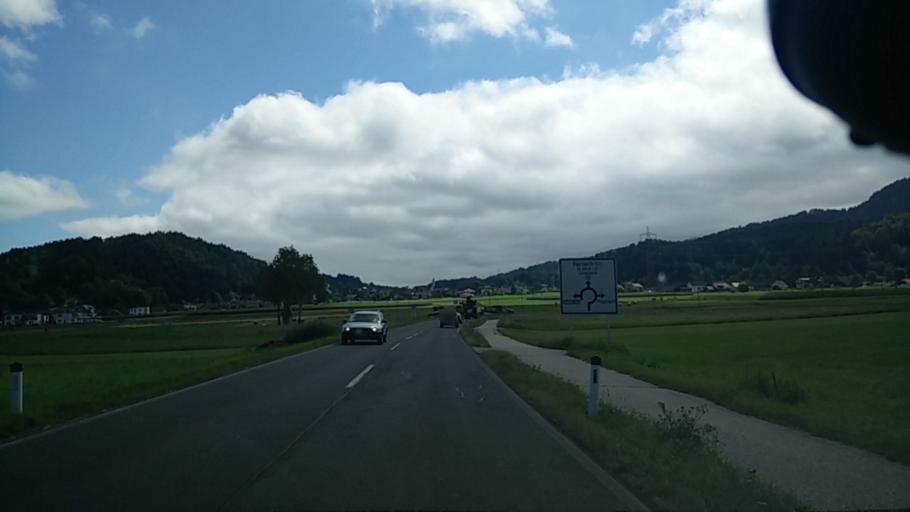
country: AT
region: Carinthia
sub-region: Politischer Bezirk Villach Land
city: Finkenstein am Faaker See
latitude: 46.5603
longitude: 13.9051
